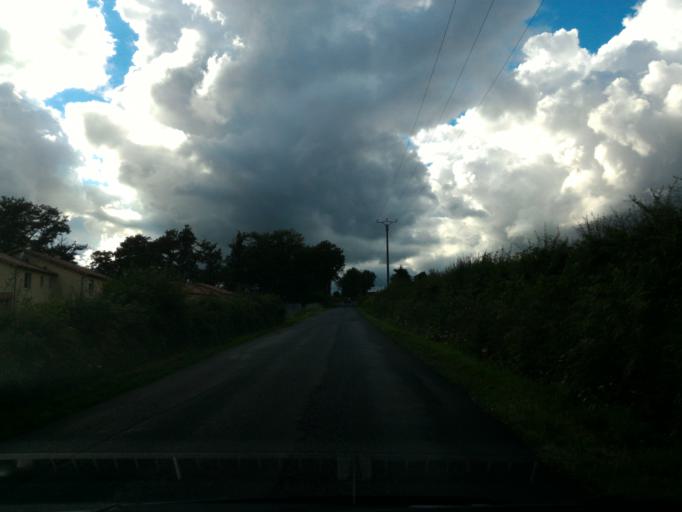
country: FR
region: Limousin
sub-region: Departement de la Haute-Vienne
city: Saint-Junien
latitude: 45.9243
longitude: 0.9359
